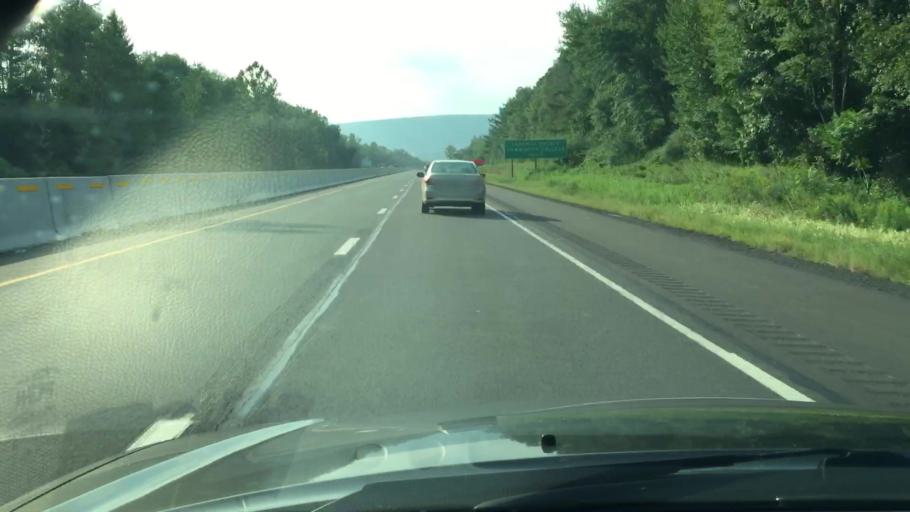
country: US
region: Pennsylvania
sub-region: Luzerne County
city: Nanticoke
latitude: 41.2013
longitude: -75.9697
